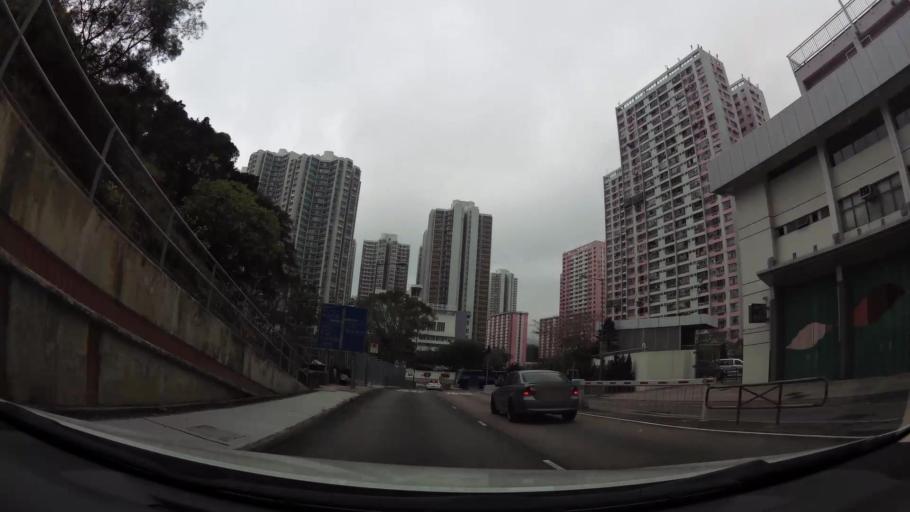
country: HK
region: Central and Western
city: Central
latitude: 22.2432
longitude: 114.1522
